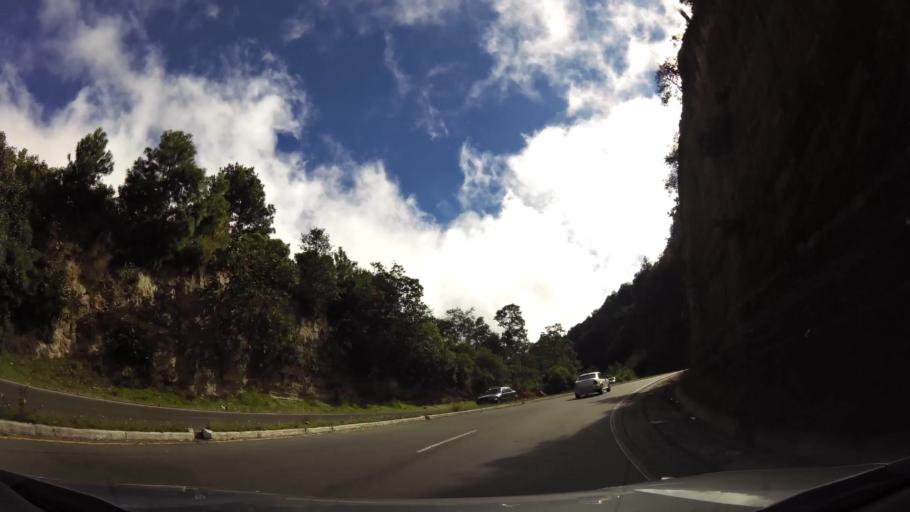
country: GT
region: Solola
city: Santa Catarina Ixtahuacan
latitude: 14.8443
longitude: -91.3817
